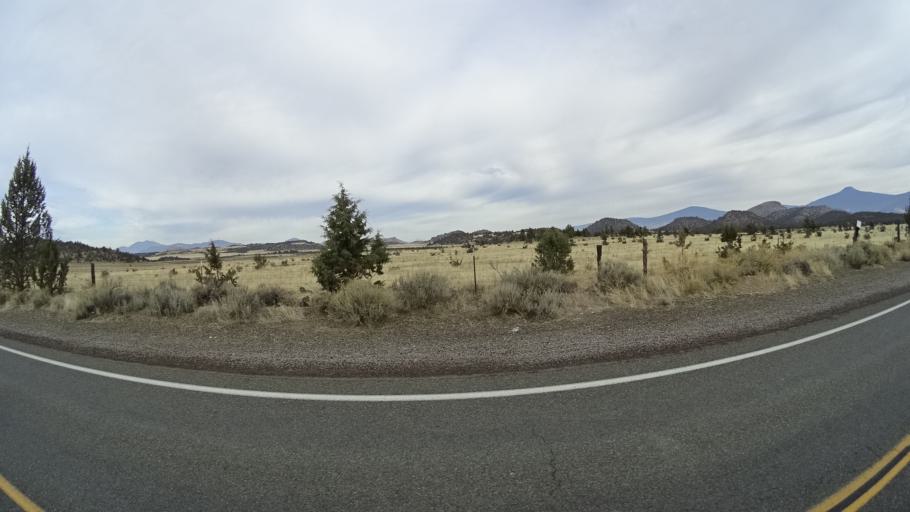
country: US
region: California
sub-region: Siskiyou County
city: Montague
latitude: 41.6402
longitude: -122.4703
